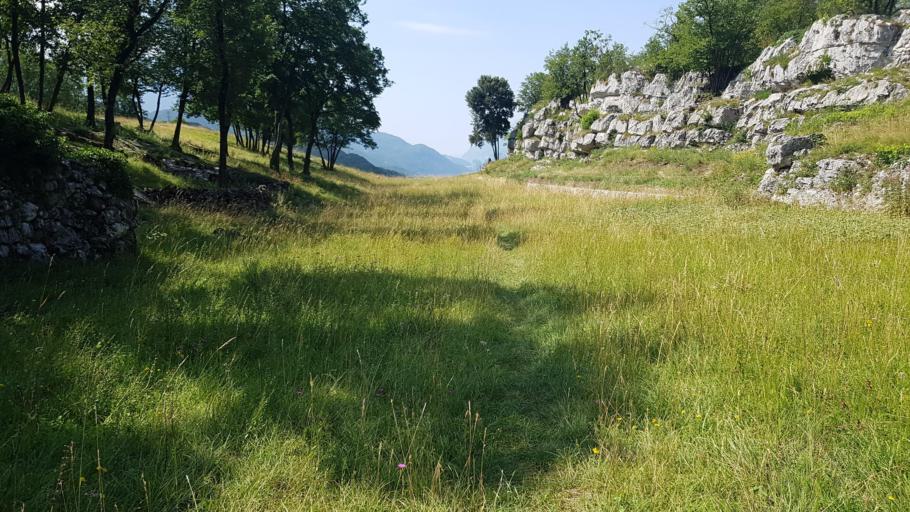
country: IT
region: Trentino-Alto Adige
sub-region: Provincia di Trento
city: Lasino
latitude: 46.0276
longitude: 10.9729
